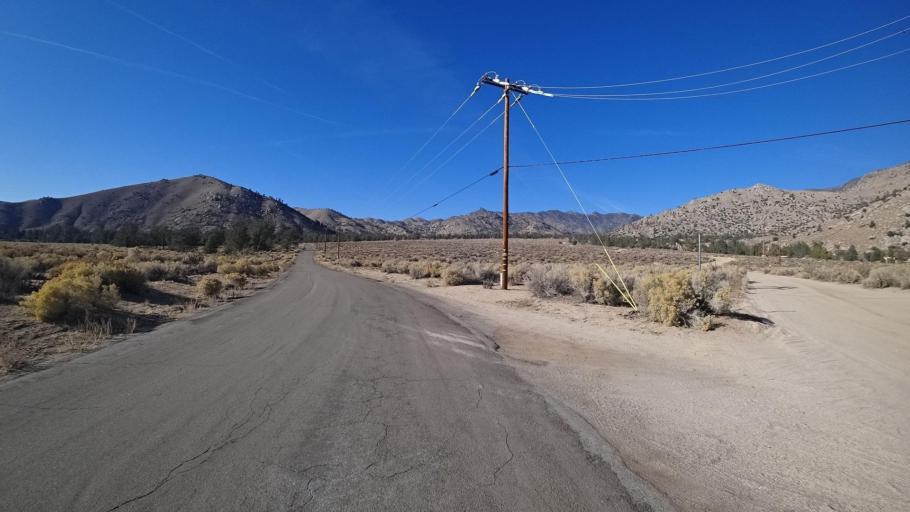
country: US
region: California
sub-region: Kern County
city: Weldon
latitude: 35.6926
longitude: -118.2904
